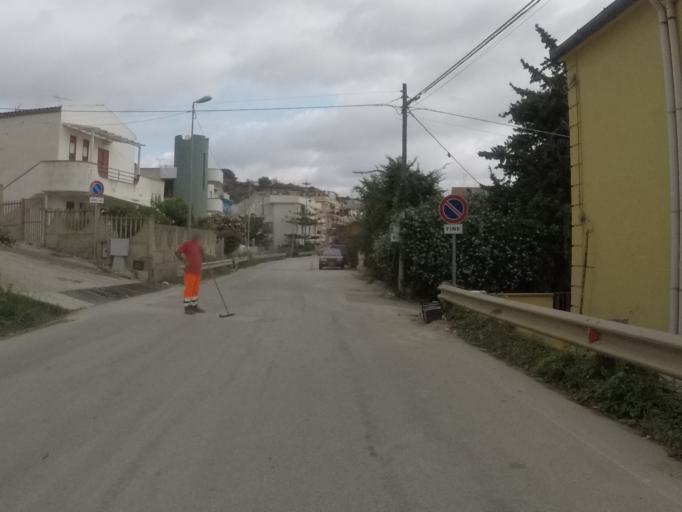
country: IT
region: Sicily
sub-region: Agrigento
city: Realmonte
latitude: 37.2895
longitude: 13.4823
